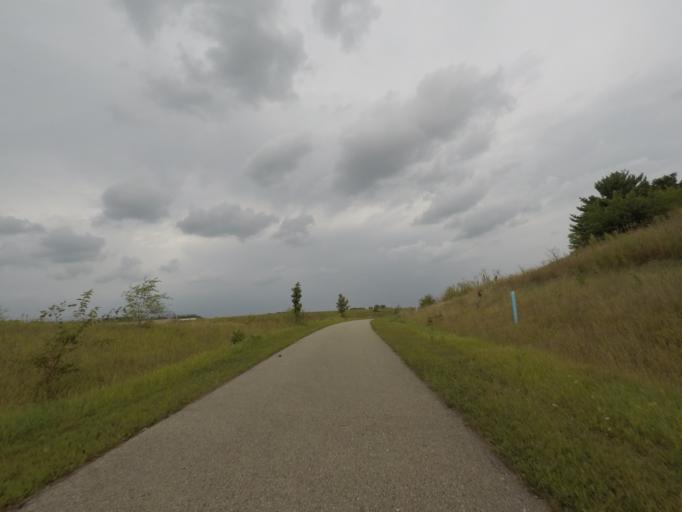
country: US
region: Wisconsin
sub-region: Jefferson County
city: Jefferson
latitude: 42.9849
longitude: -88.8289
